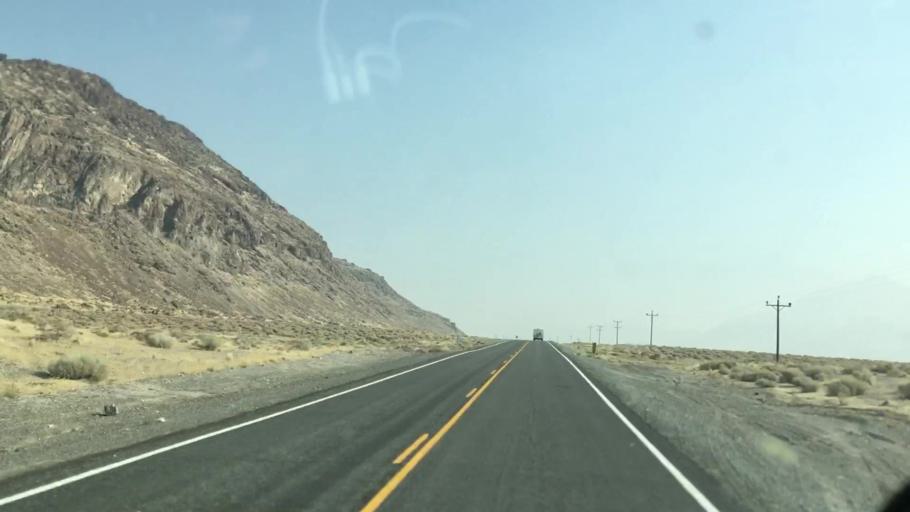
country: US
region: Nevada
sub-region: Lyon County
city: Fernley
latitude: 40.3151
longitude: -119.3488
